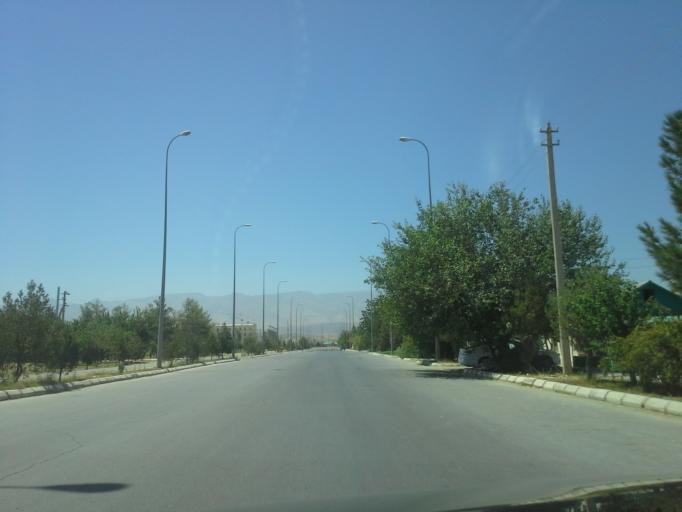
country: TM
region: Ahal
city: Ashgabat
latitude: 38.0053
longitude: 58.3045
